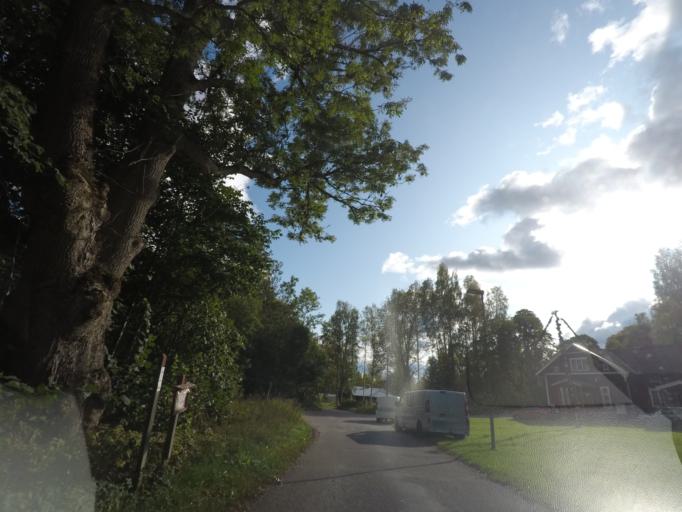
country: SE
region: Vaestmanland
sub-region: Skinnskattebergs Kommun
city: Skinnskatteberg
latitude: 59.8275
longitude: 15.6767
